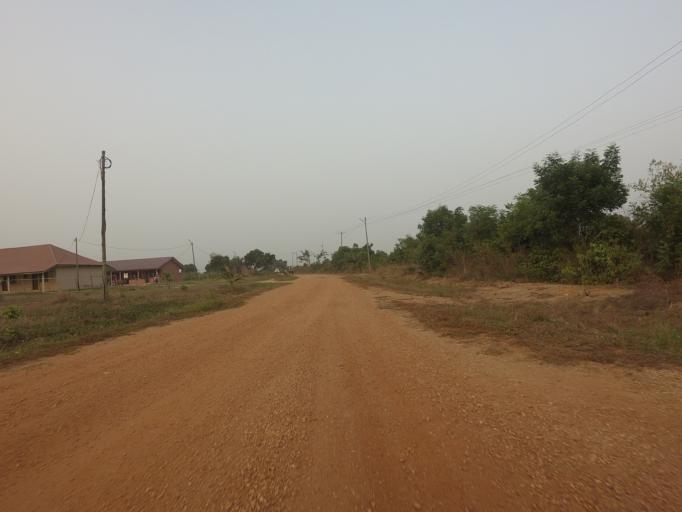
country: GH
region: Volta
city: Anloga
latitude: 5.9668
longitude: 0.6215
